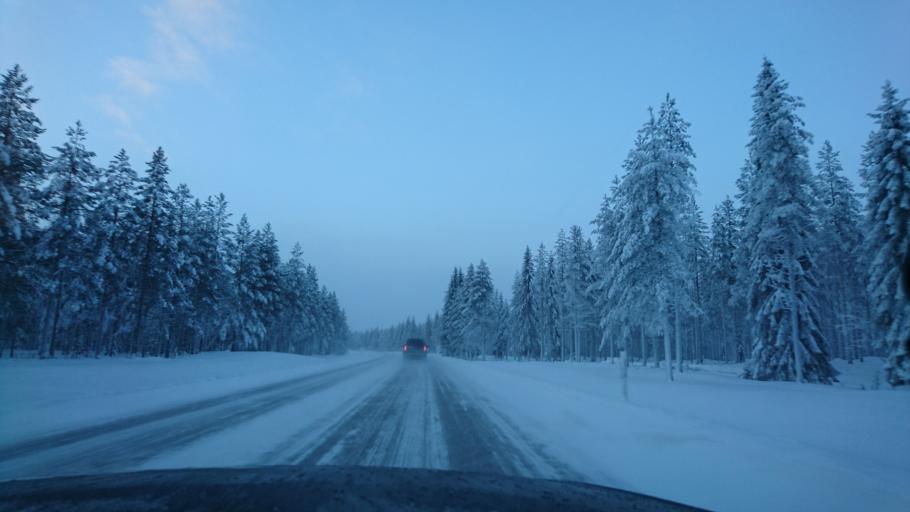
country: FI
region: Northern Ostrobothnia
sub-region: Koillismaa
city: Taivalkoski
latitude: 65.4757
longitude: 27.7537
